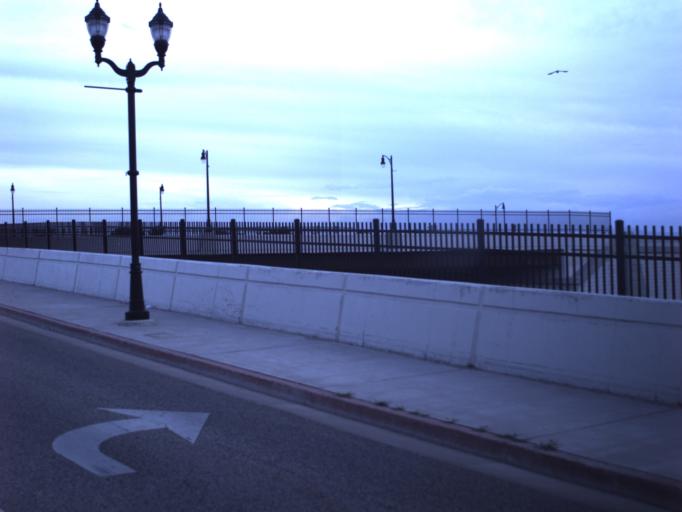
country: US
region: Utah
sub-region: Davis County
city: Layton
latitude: 41.0566
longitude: -111.9640
